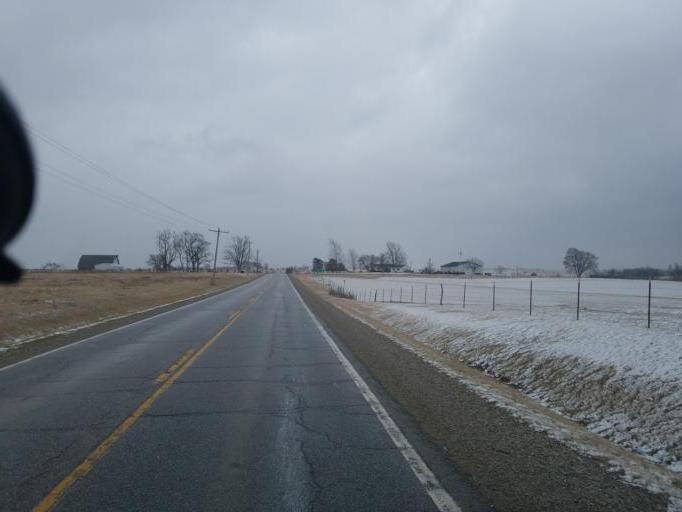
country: US
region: Missouri
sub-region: Putnam County
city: Unionville
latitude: 40.4723
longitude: -92.9635
